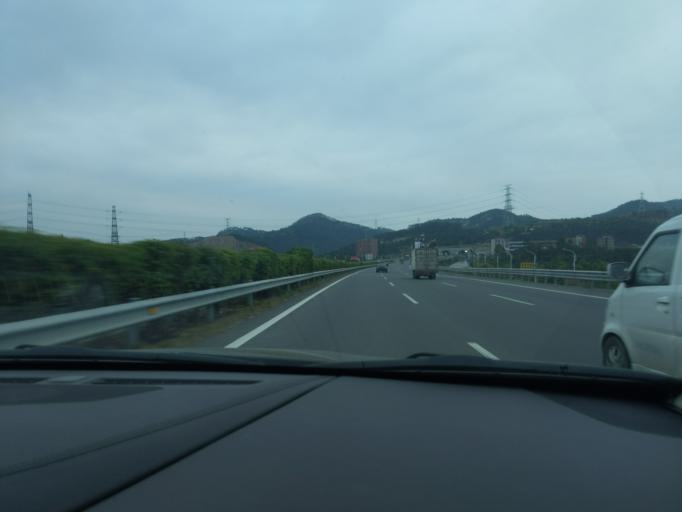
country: CN
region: Fujian
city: Cizao
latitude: 24.7813
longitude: 118.5045
